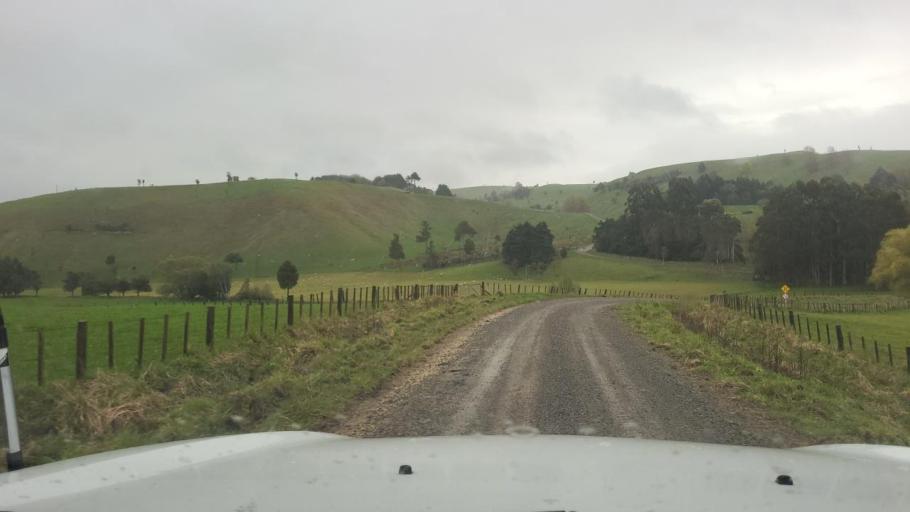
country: NZ
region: Wellington
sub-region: Masterton District
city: Masterton
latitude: -41.0727
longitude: 175.7261
